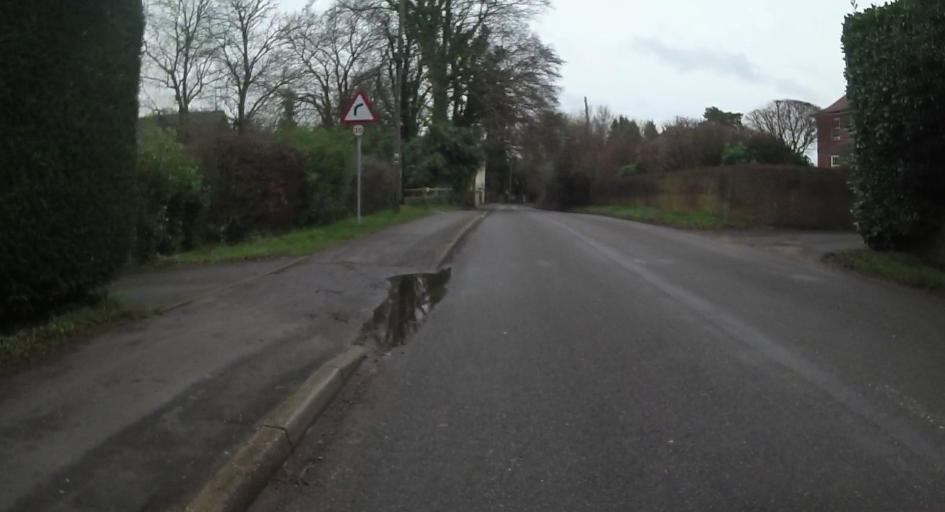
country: GB
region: England
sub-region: Hampshire
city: Four Marks
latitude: 51.1025
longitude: -1.0490
